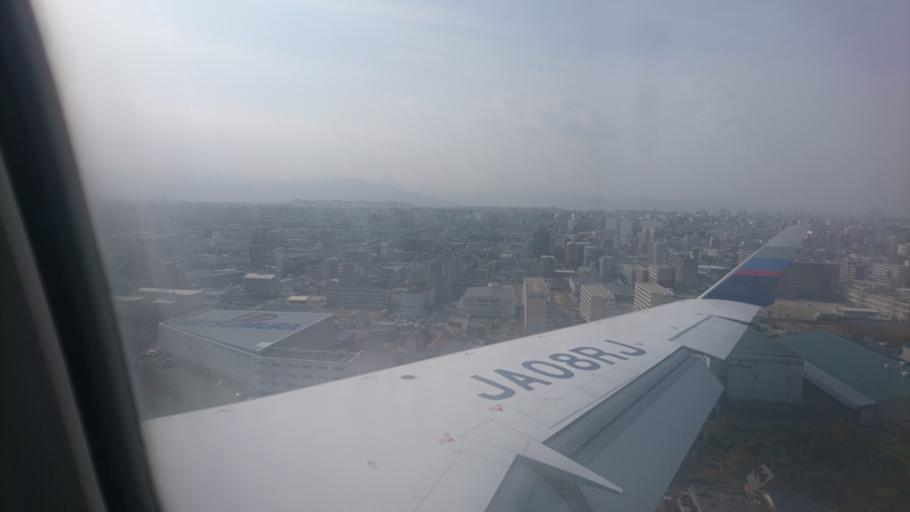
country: JP
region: Fukuoka
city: Fukuoka-shi
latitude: 33.6050
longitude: 130.4375
